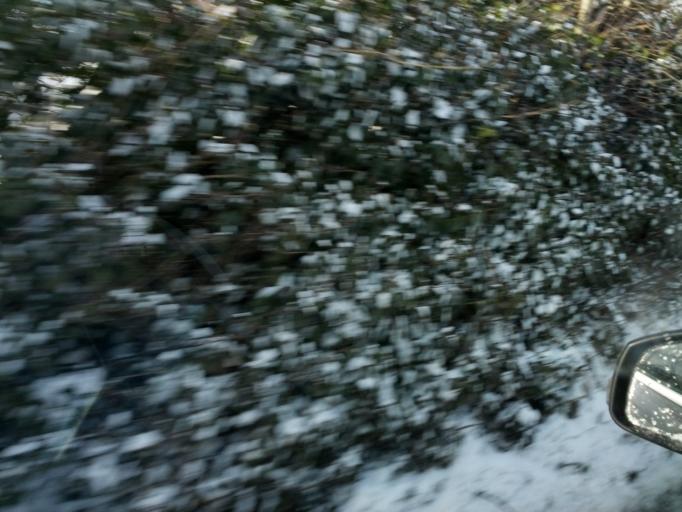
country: IE
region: Connaught
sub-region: County Galway
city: Athenry
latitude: 53.2229
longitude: -8.7409
